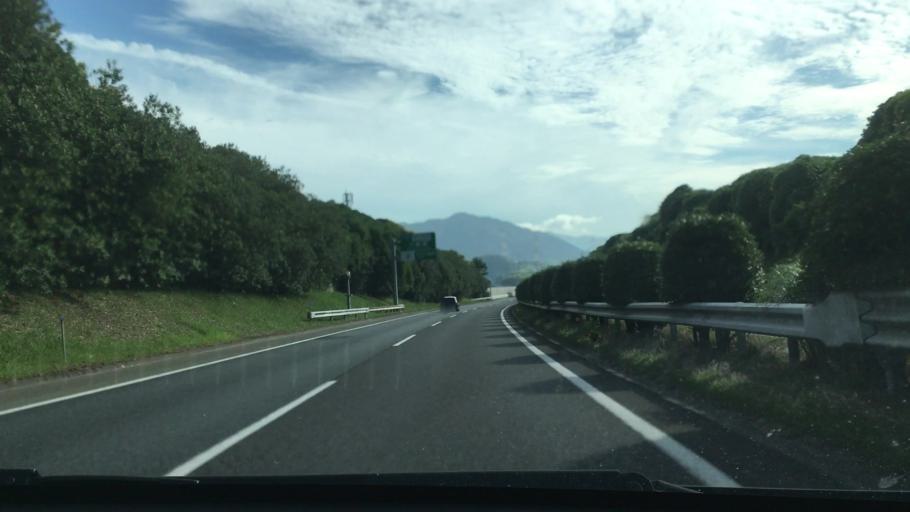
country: JP
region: Fukuoka
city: Kanda
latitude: 33.8383
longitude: 130.9252
